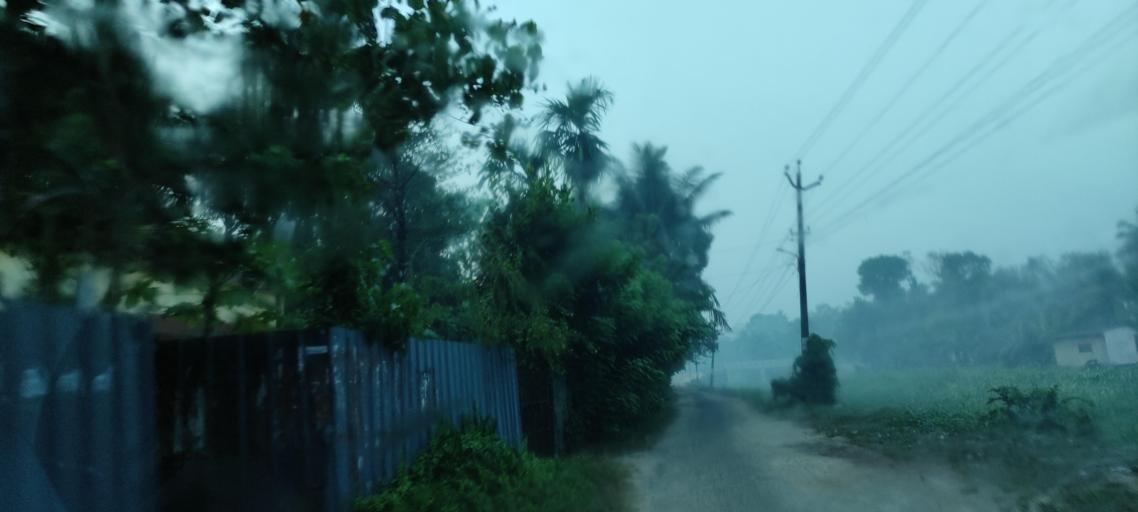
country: IN
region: Kerala
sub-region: Alappuzha
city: Alleppey
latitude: 9.5304
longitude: 76.3294
